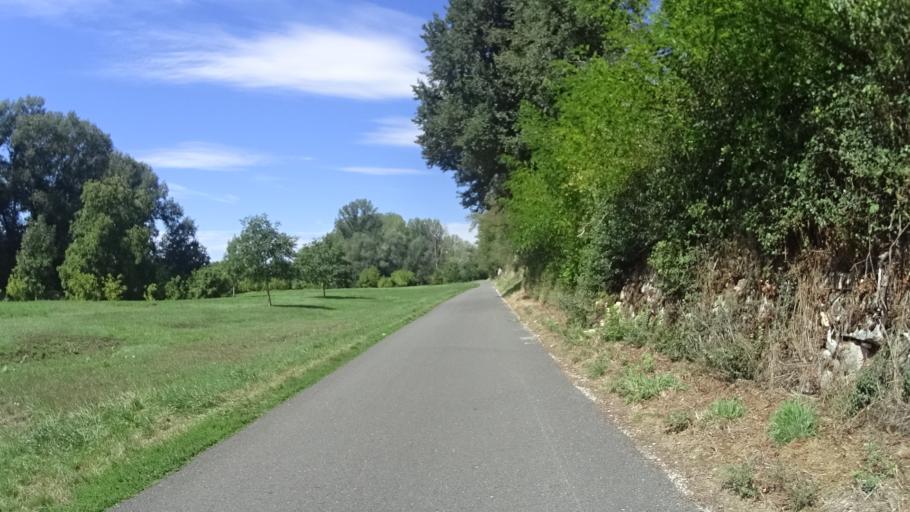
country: FR
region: Centre
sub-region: Departement du Loiret
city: Bonny-sur-Loire
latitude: 47.5725
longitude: 2.8207
